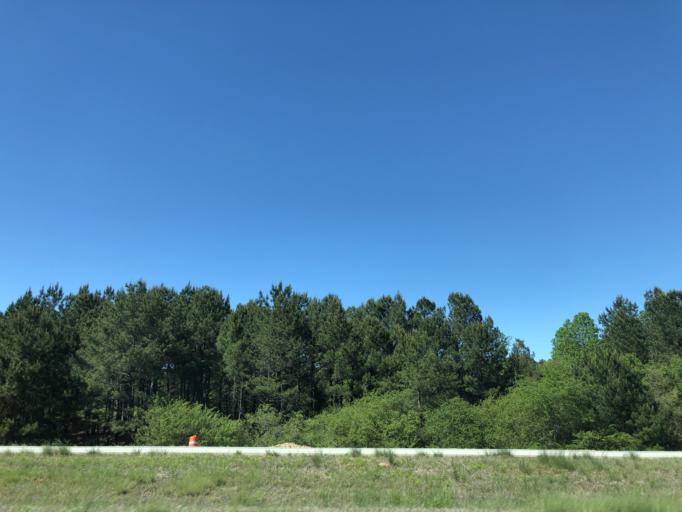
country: US
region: Georgia
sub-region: Gwinnett County
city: Dacula
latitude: 33.9732
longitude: -83.8630
